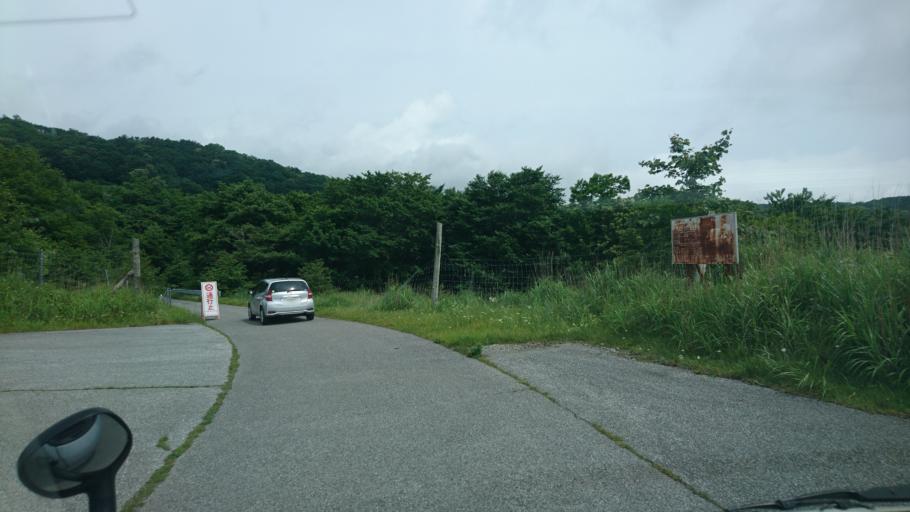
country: JP
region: Iwate
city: Ofunato
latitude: 39.1716
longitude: 141.7611
